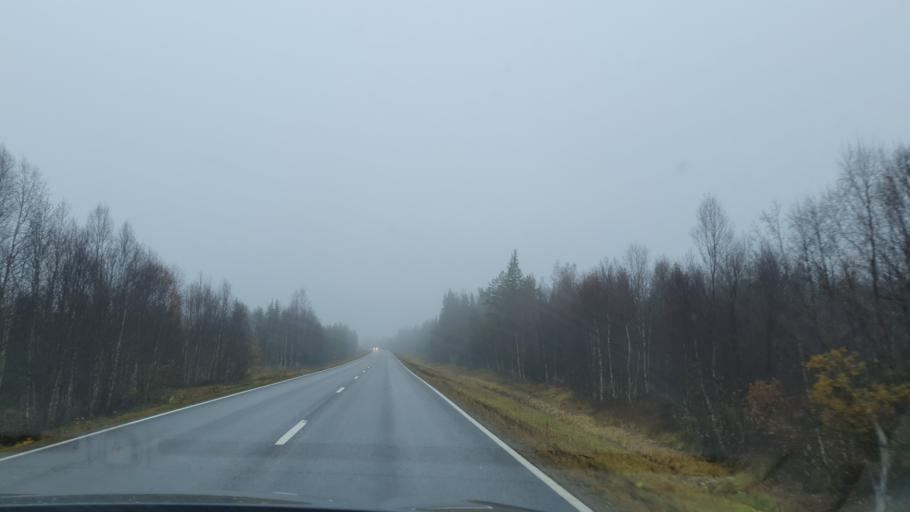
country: FI
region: Lapland
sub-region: Tunturi-Lappi
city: Kittilae
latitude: 67.5427
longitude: 24.9127
